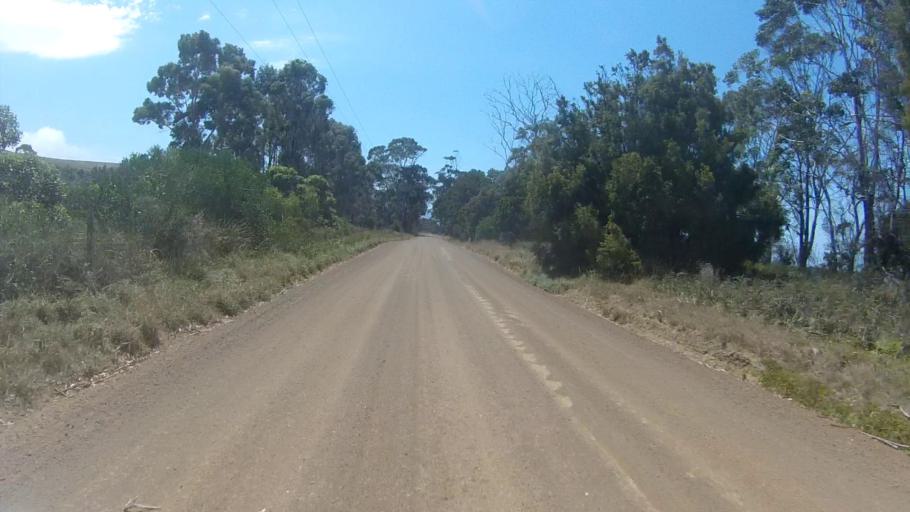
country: AU
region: Tasmania
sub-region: Sorell
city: Sorell
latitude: -42.8355
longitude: 147.8547
